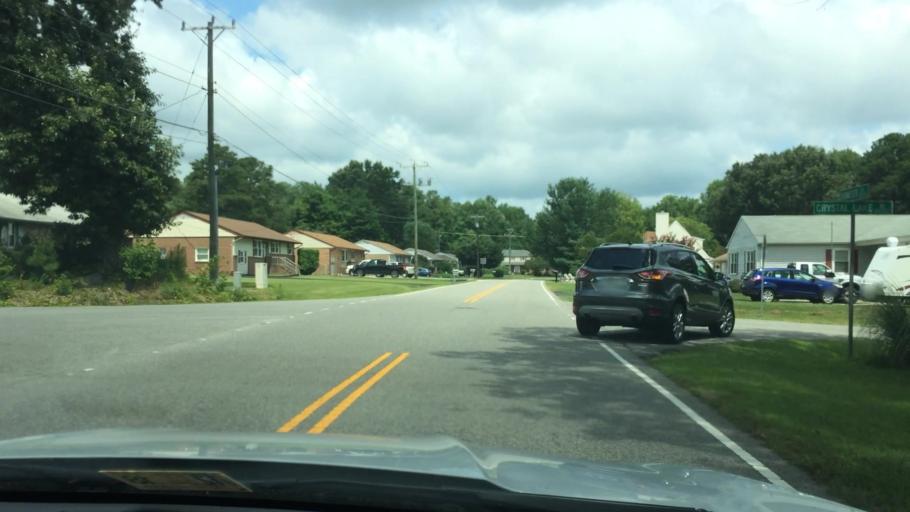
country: US
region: Virginia
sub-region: City of Poquoson
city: Poquoson
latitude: 37.1494
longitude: -76.4494
